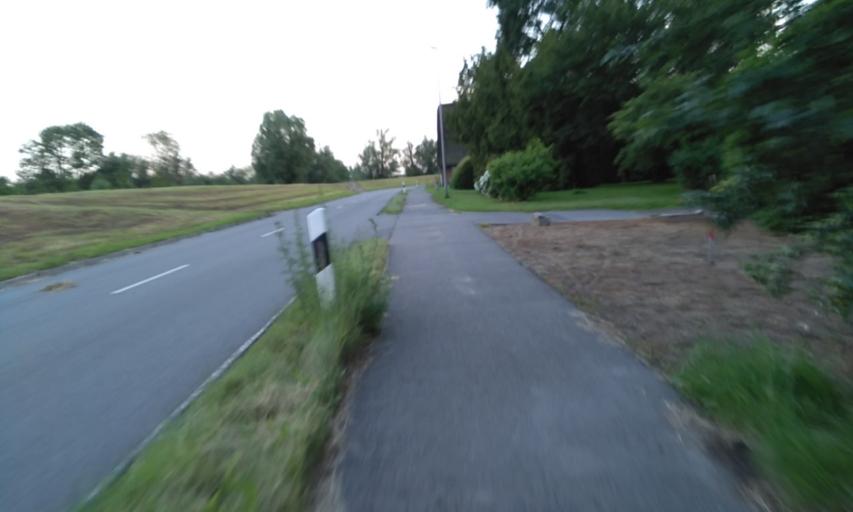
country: DE
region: Lower Saxony
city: Buxtehude
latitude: 53.4966
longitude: 9.7174
